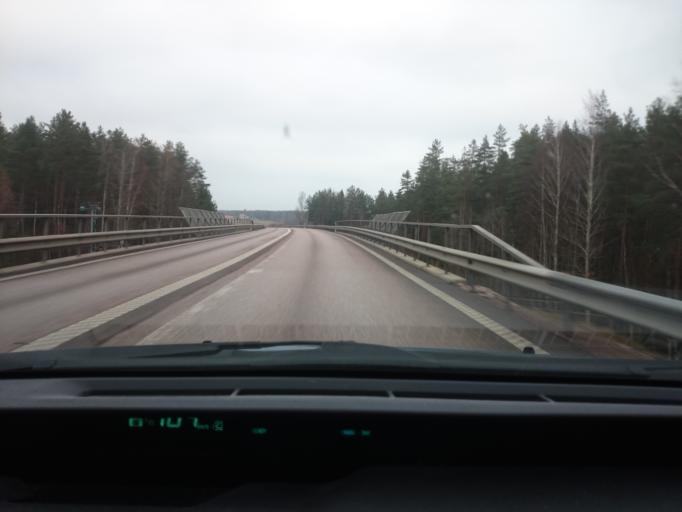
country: SE
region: Dalarna
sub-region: Avesta Kommun
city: Avesta
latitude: 60.0885
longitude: 16.3200
